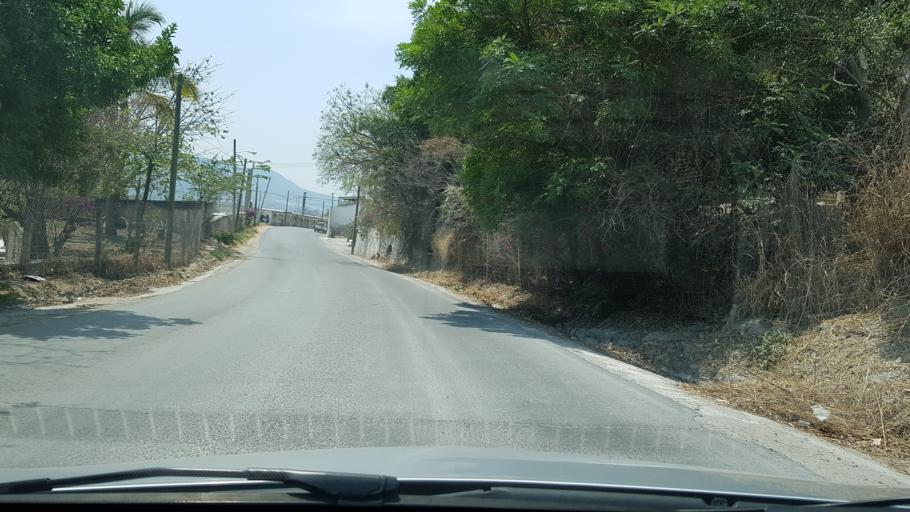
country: MX
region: Morelos
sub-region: Jiutepec
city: Jiutepec
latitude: 18.8701
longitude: -99.1737
